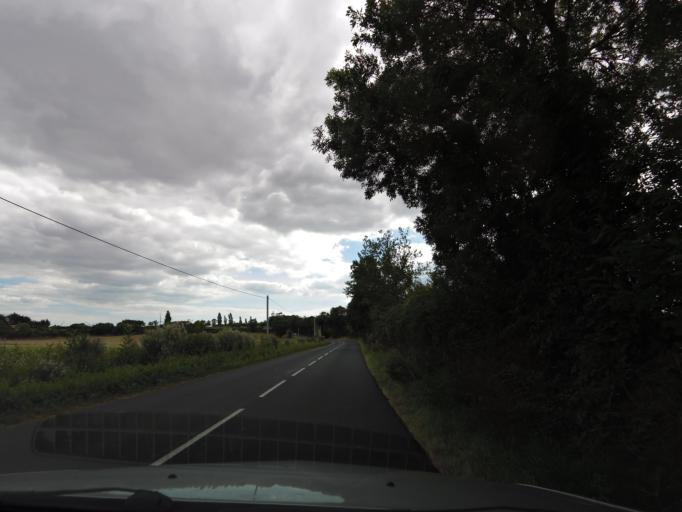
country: FR
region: Pays de la Loire
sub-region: Departement de la Vendee
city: Avrille
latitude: 46.4470
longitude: -1.4625
